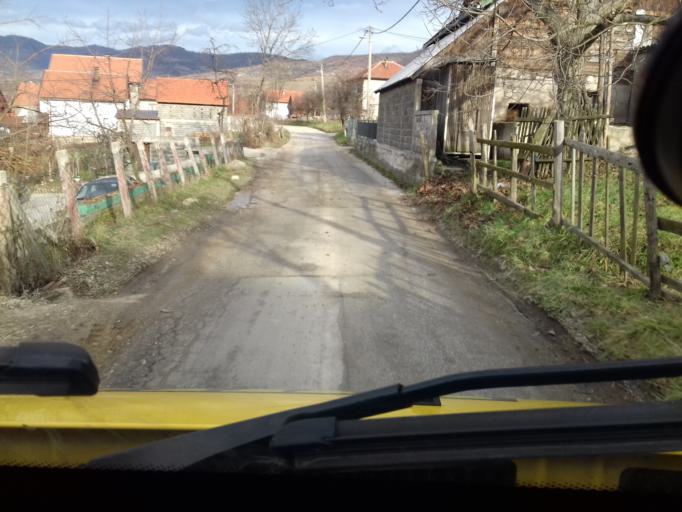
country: BA
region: Federation of Bosnia and Herzegovina
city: Zenica
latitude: 44.1636
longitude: 17.9719
